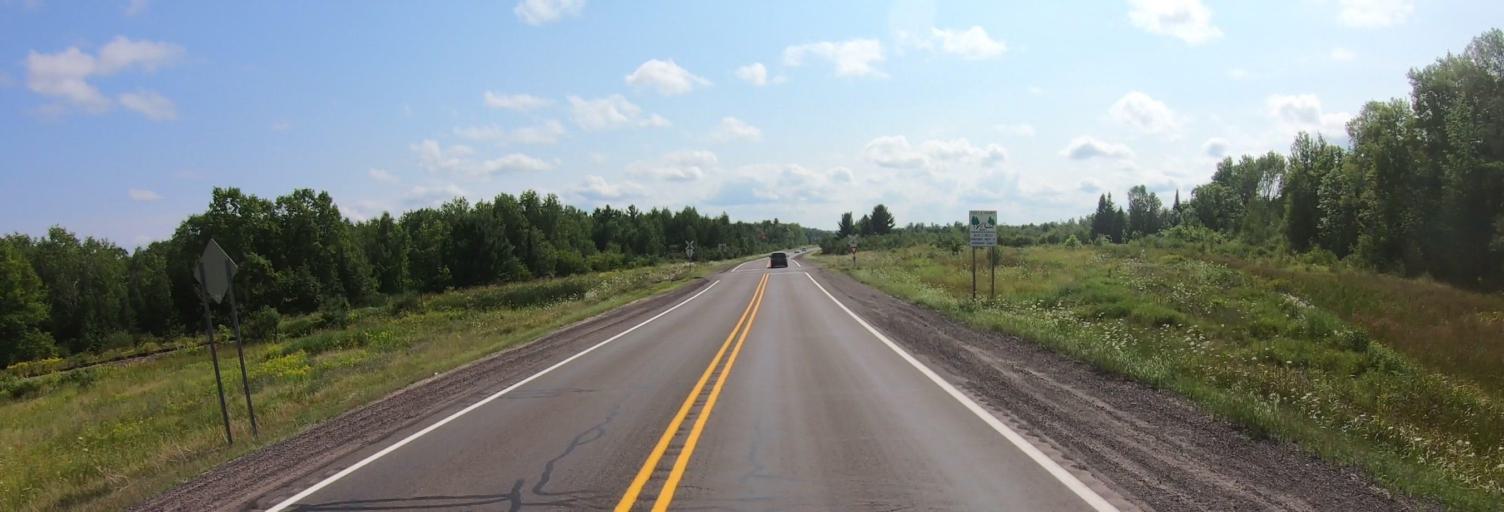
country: US
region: Michigan
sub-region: Ontonagon County
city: Ontonagon
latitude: 46.7289
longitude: -89.1486
